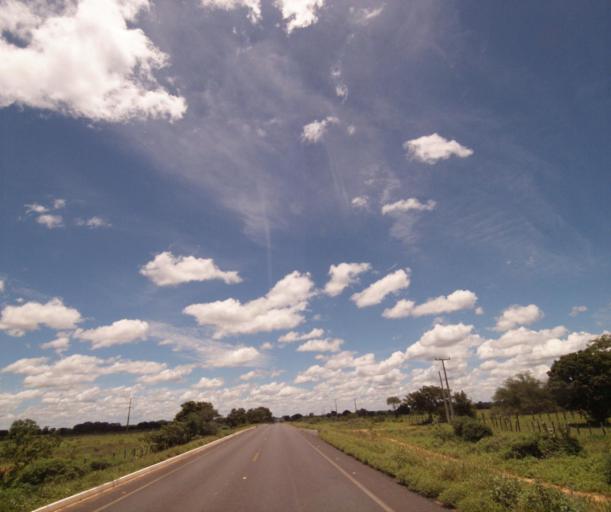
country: BR
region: Bahia
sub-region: Bom Jesus Da Lapa
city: Bom Jesus da Lapa
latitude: -13.2606
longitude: -43.5090
